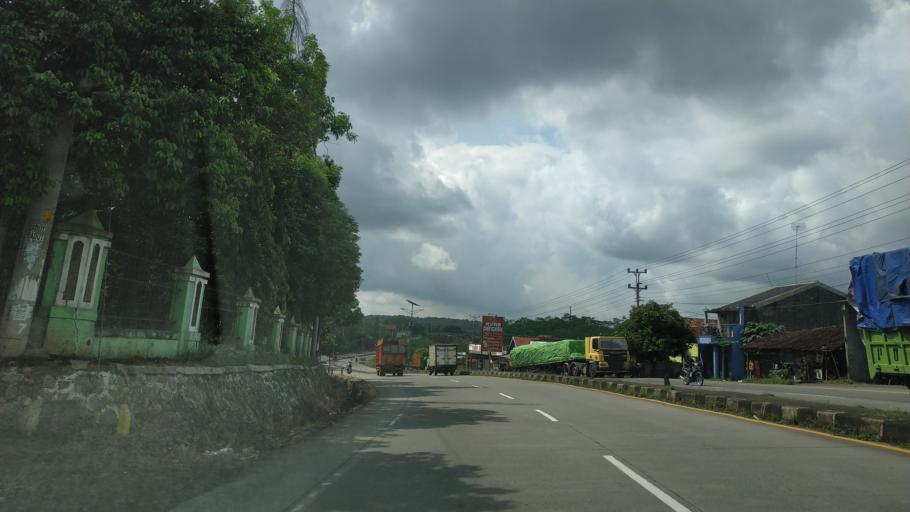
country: ID
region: Central Java
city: Pekalongan
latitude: -6.9506
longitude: 109.8278
